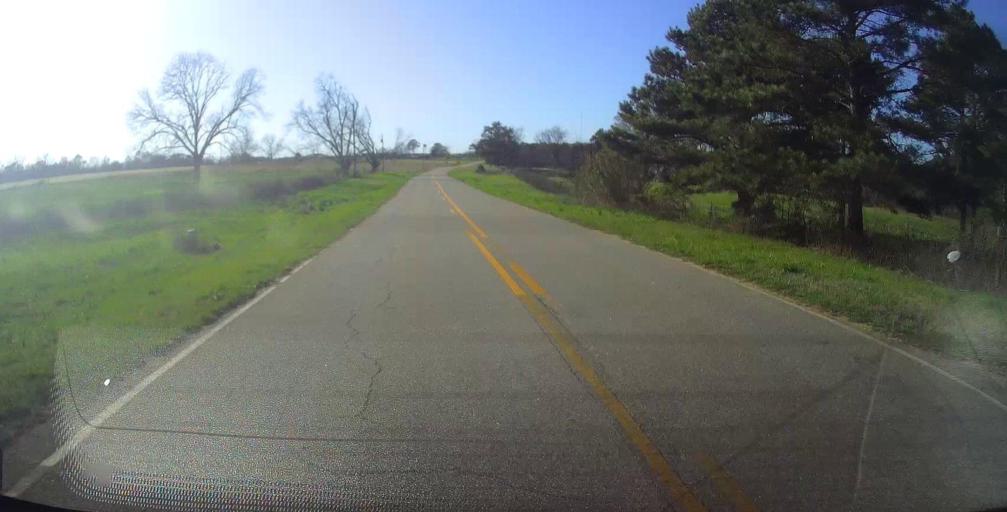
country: US
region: Georgia
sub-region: Houston County
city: Perry
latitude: 32.3684
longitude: -83.6972
